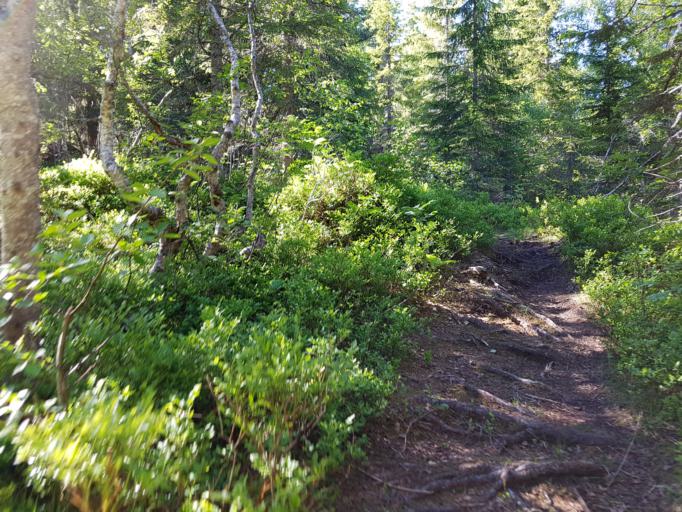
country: NO
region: Sor-Trondelag
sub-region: Trondheim
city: Trondheim
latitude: 63.4084
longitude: 10.3145
